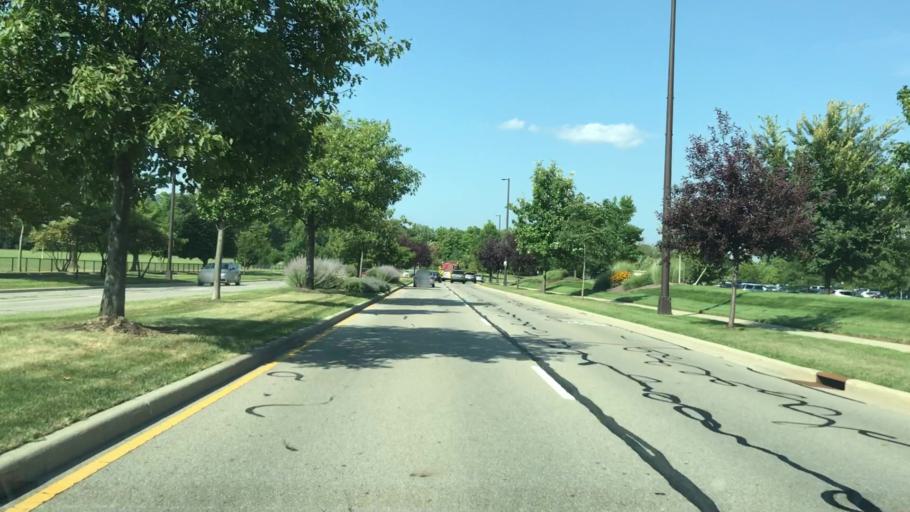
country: US
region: Ohio
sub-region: Franklin County
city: Dublin
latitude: 40.1084
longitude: -83.1265
